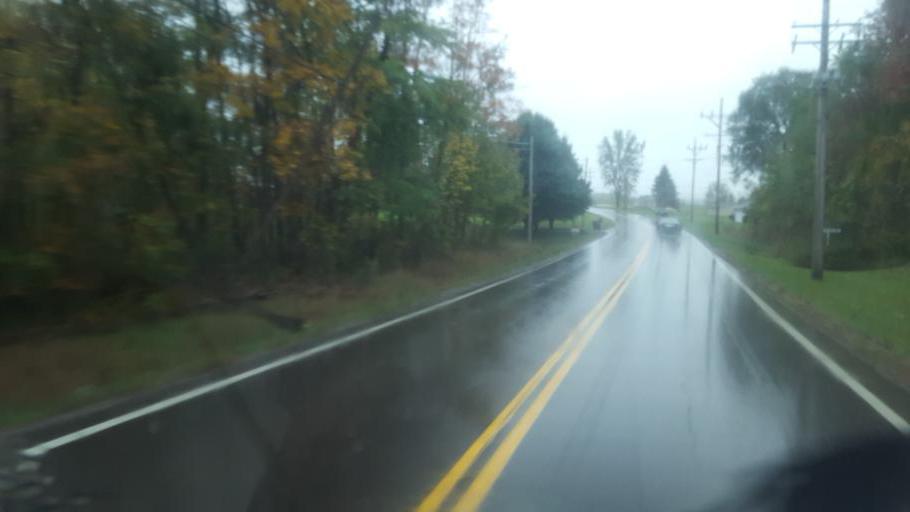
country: US
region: Ohio
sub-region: Richland County
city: Lincoln Heights
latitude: 40.8140
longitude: -82.4902
